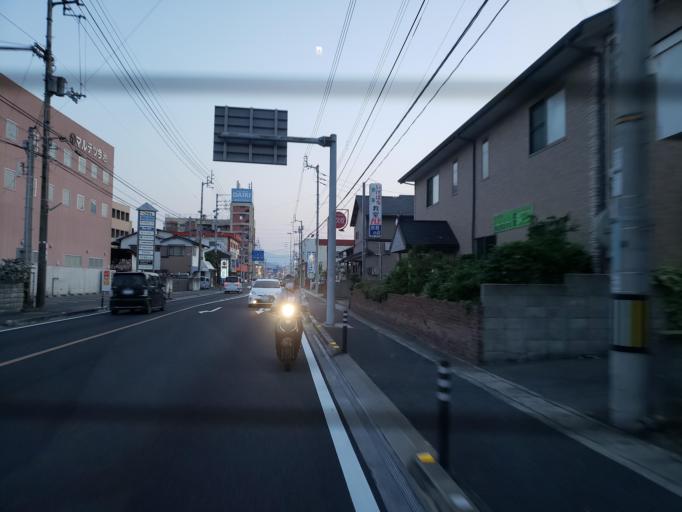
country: JP
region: Ehime
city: Hojo
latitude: 34.0527
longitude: 132.9850
